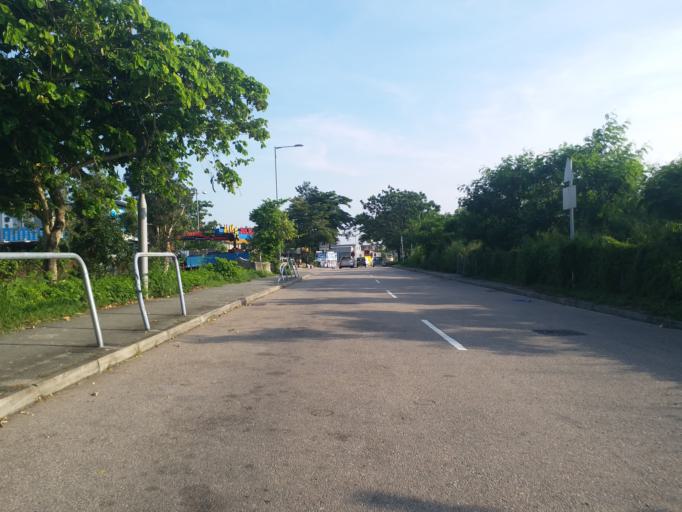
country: HK
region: Yuen Long
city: Yuen Long Kau Hui
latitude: 22.4740
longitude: 114.0514
